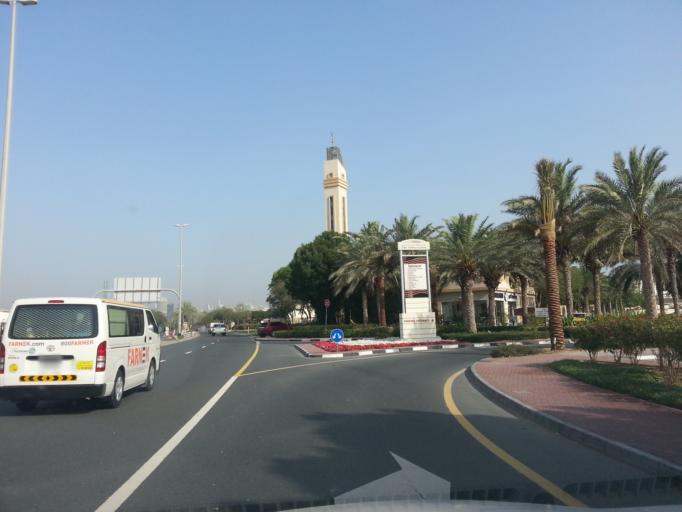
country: AE
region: Dubai
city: Dubai
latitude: 25.0529
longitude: 55.1704
